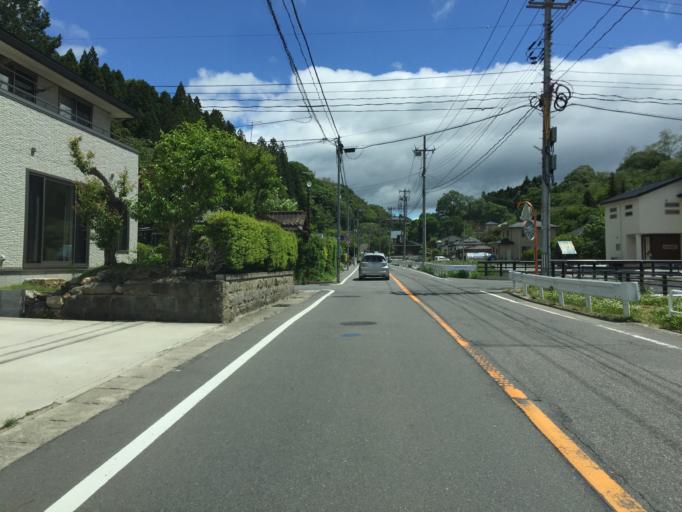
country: JP
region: Fukushima
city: Miharu
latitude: 37.4394
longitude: 140.4992
